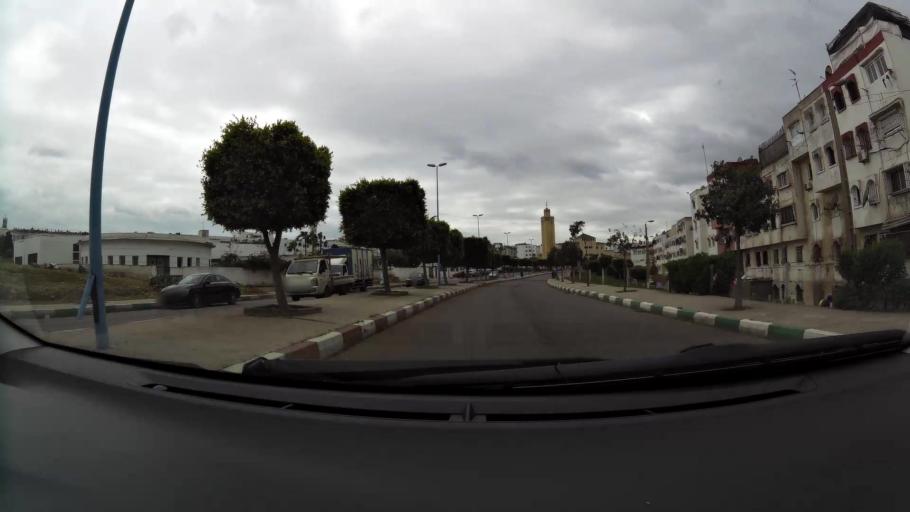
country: MA
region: Grand Casablanca
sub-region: Casablanca
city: Casablanca
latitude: 33.5907
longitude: -7.5521
